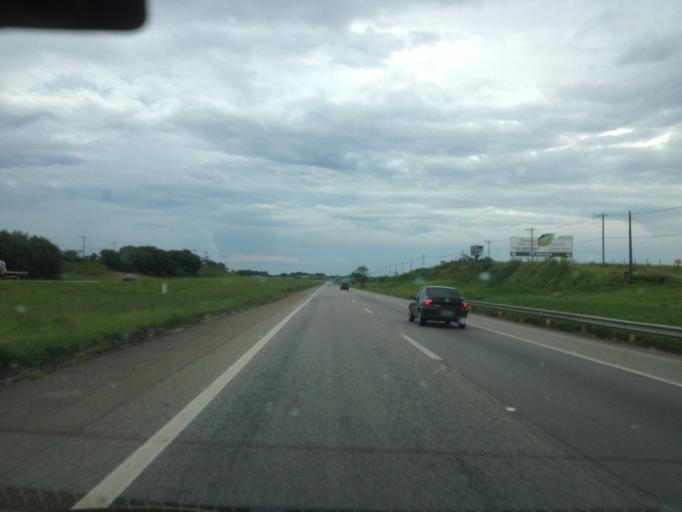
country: BR
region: Sao Paulo
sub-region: Boituva
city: Boituva
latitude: -23.3182
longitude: -47.6221
